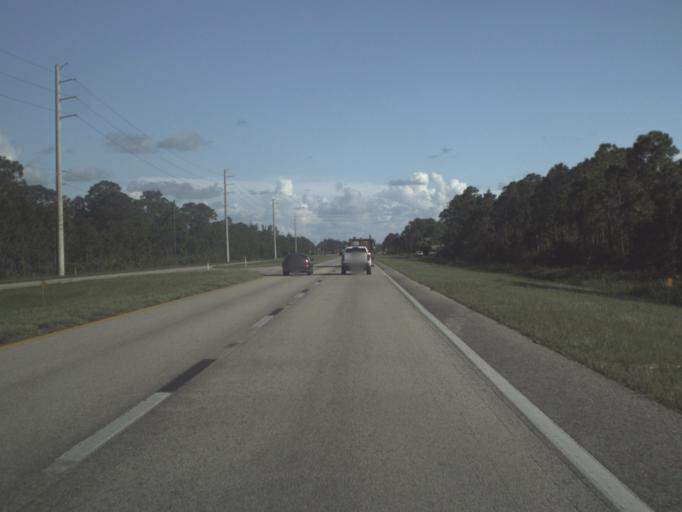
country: US
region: Florida
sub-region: Charlotte County
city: Charlotte Park
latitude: 26.8641
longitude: -81.9948
